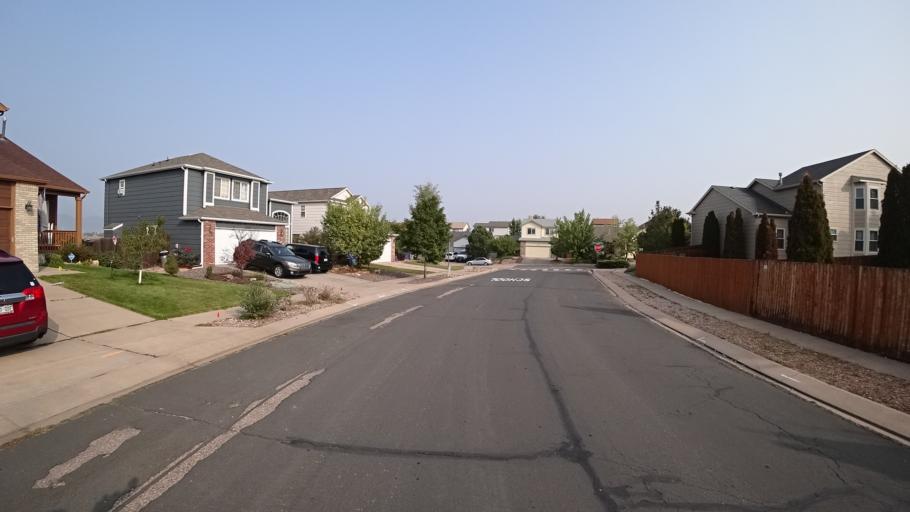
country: US
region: Colorado
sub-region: El Paso County
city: Black Forest
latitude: 38.9358
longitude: -104.7303
